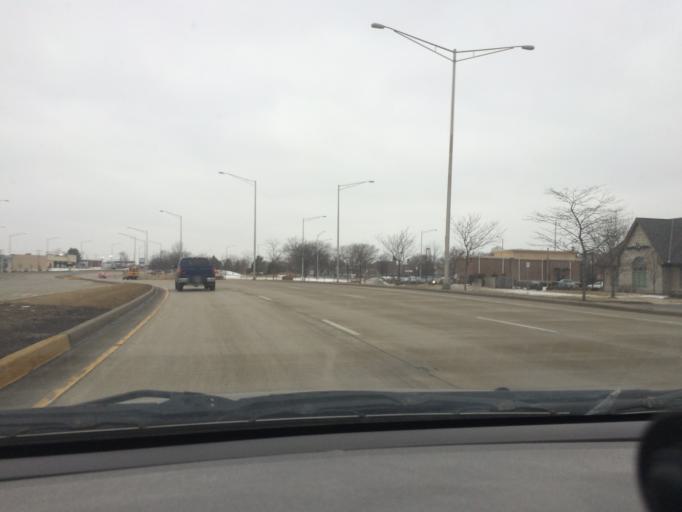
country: US
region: Illinois
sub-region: Cook County
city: Hoffman Estates
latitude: 42.0478
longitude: -88.0910
